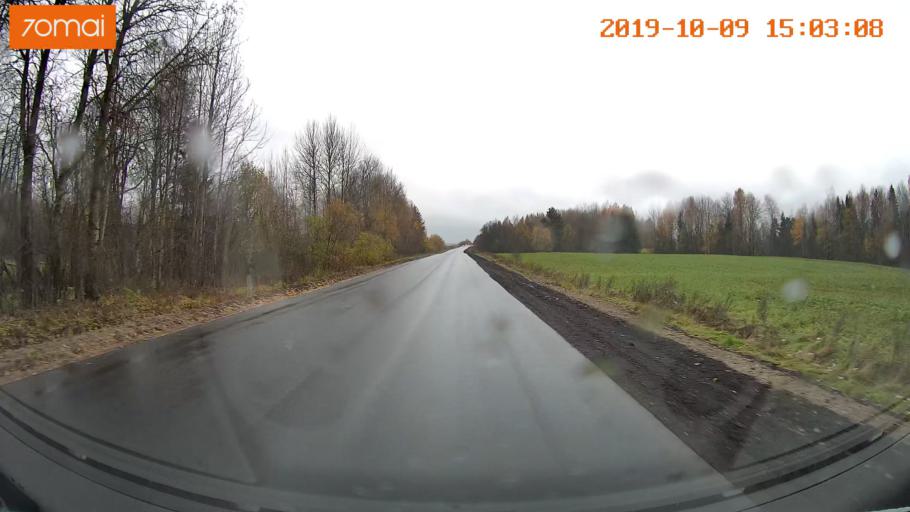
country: RU
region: Kostroma
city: Chistyye Bory
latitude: 58.2756
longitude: 41.6763
